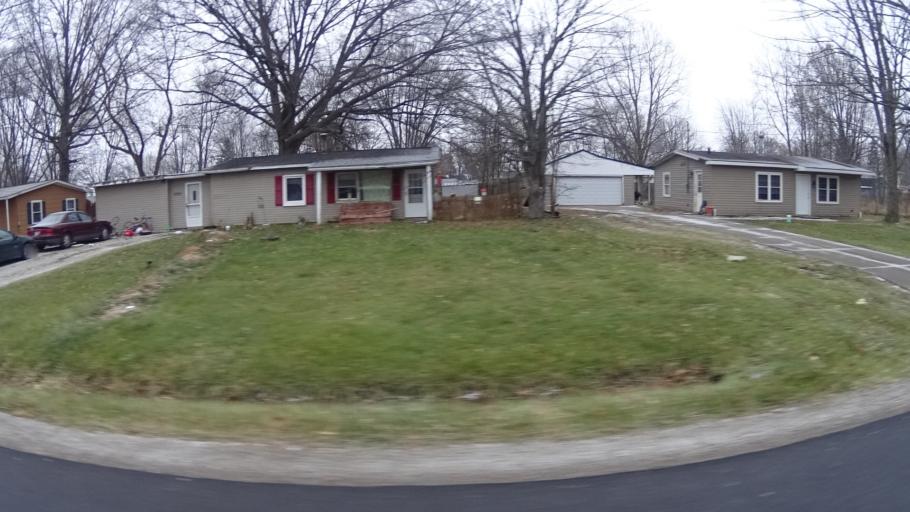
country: US
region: Ohio
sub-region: Lorain County
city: Eaton Estates
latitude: 41.3099
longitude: -82.0042
